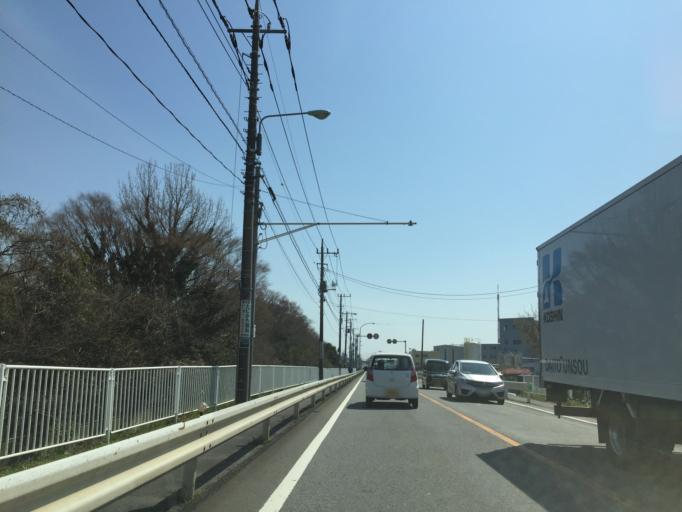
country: JP
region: Saitama
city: Shiki
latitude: 35.8597
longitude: 139.6056
